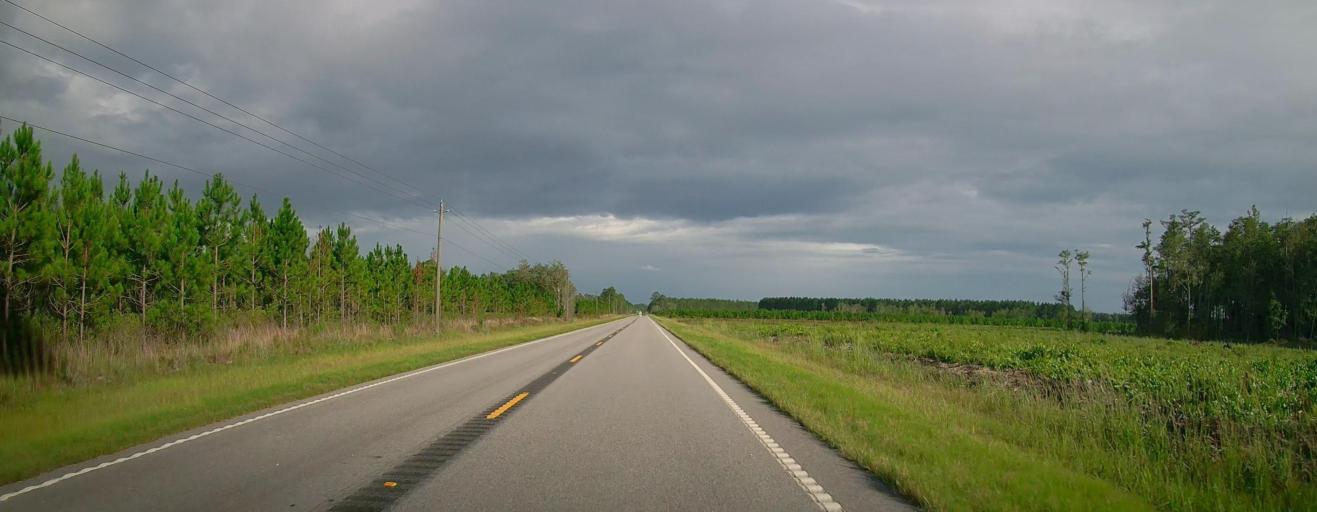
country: US
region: Georgia
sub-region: Coffee County
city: Nicholls
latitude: 31.3729
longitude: -82.6357
